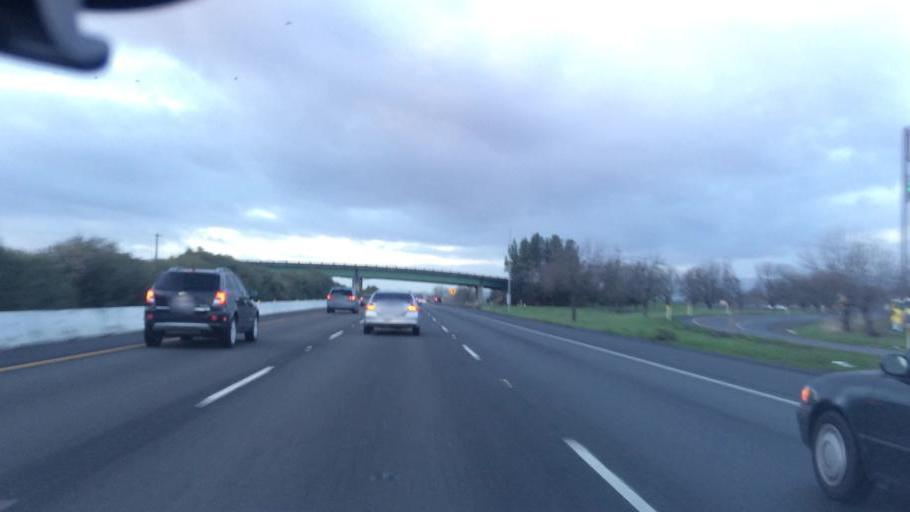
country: US
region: California
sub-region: Solano County
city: Dixon
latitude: 38.4471
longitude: -121.8573
